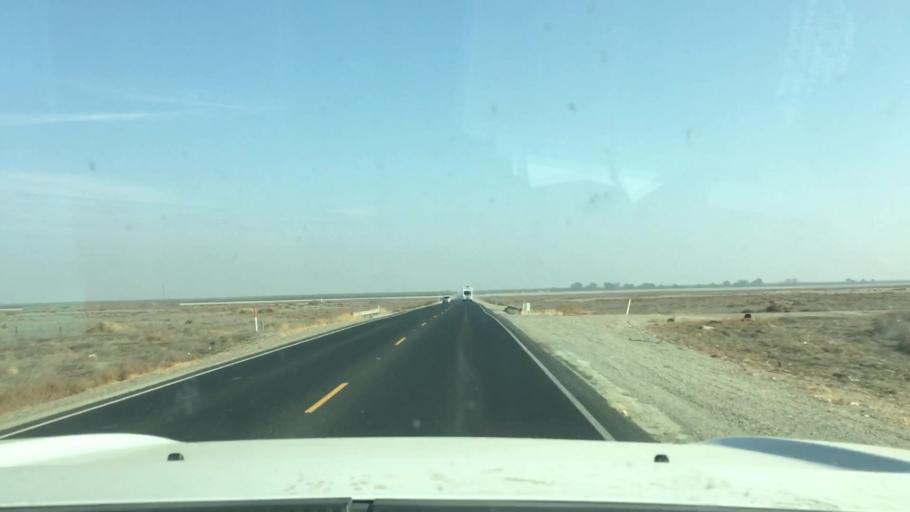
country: US
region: California
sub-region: Kern County
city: Lost Hills
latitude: 35.6159
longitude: -119.6077
